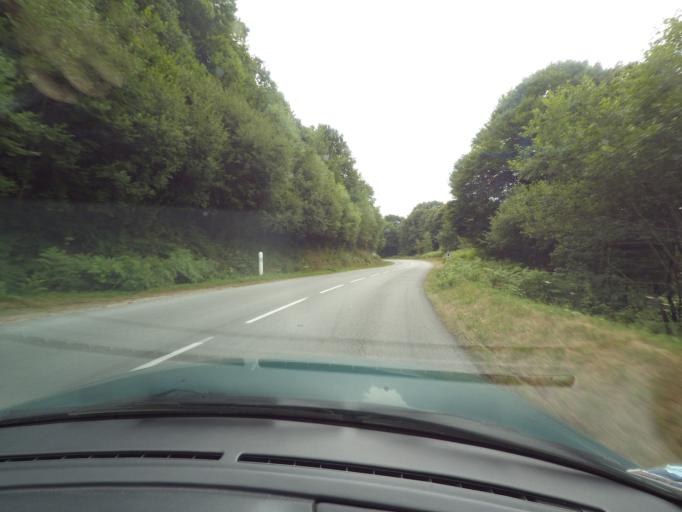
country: FR
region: Limousin
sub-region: Departement de la Haute-Vienne
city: Eymoutiers
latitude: 45.7234
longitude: 1.8015
